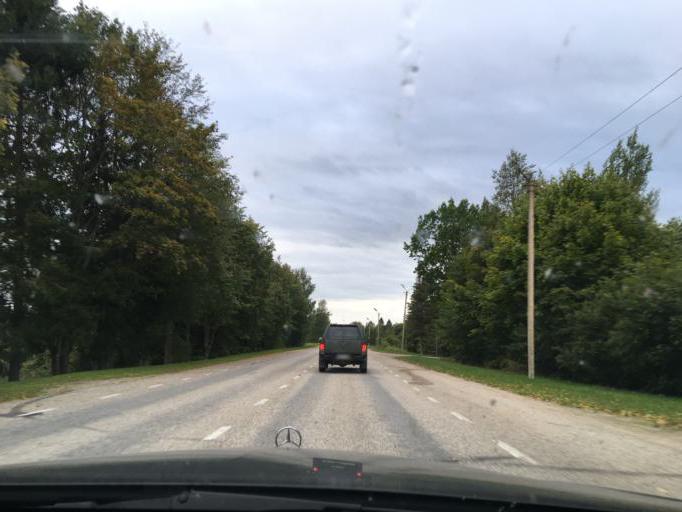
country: LV
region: Aluksnes Rajons
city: Aluksne
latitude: 57.6021
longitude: 27.2337
